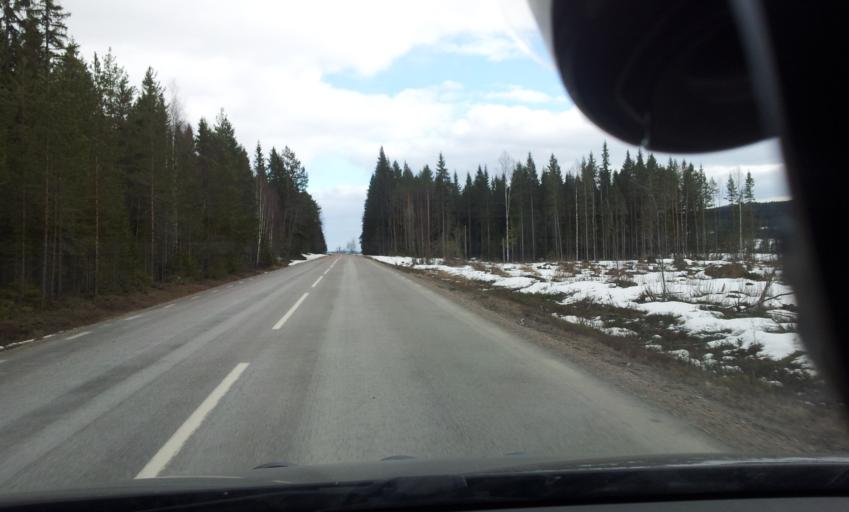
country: SE
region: Gaevleborg
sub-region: Ljusdals Kommun
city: Farila
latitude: 62.1227
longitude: 15.7214
